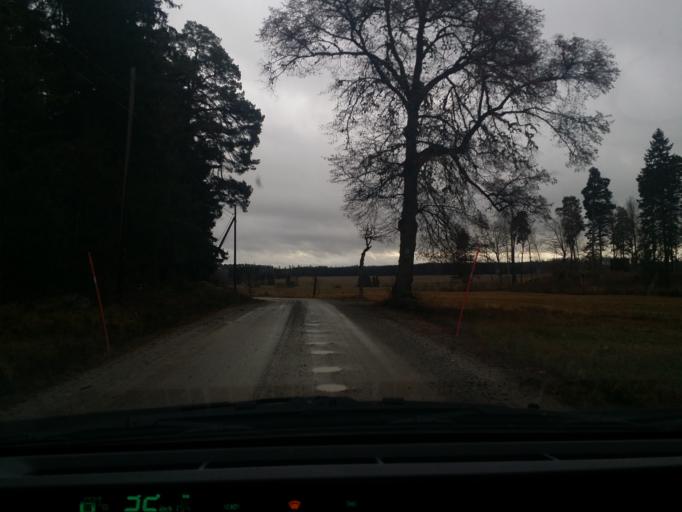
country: SE
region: Vaestmanland
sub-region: Vasteras
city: Skultuna
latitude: 59.7815
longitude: 16.3888
